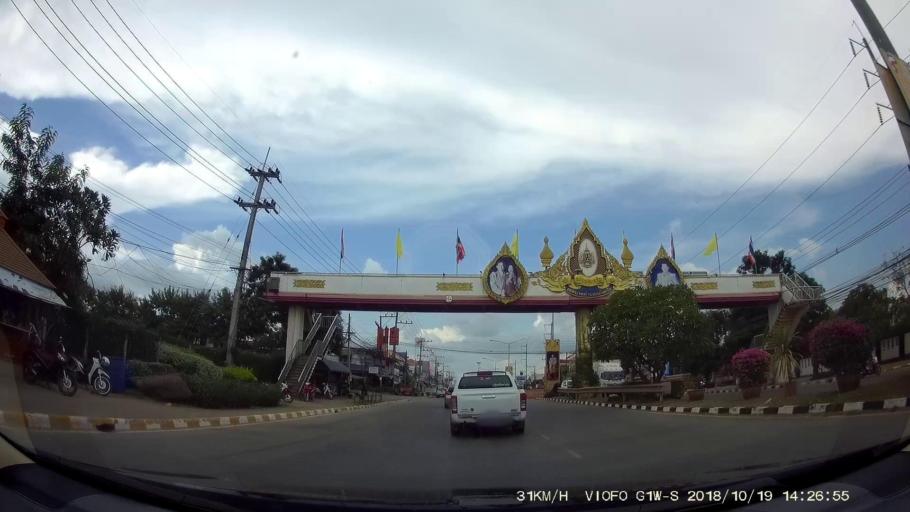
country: TH
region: Chaiyaphum
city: Kaeng Khro
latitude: 16.1094
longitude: 102.2587
